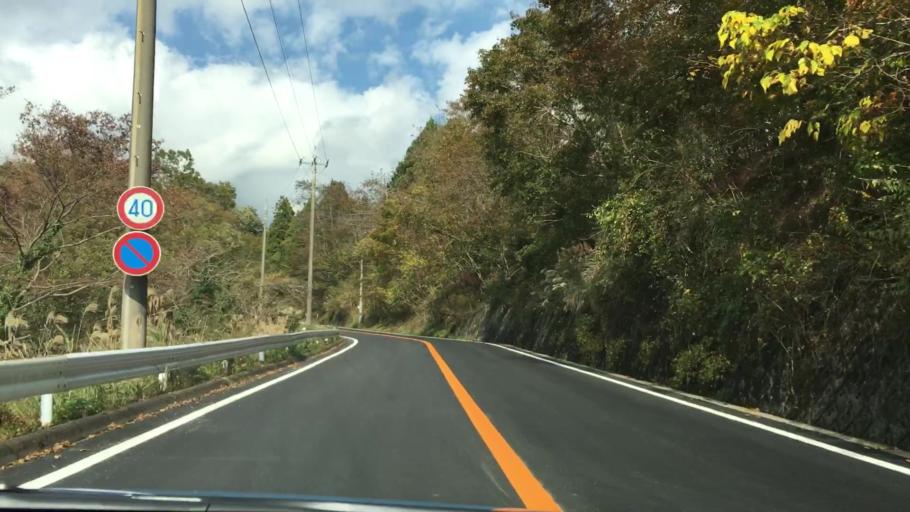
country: JP
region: Shizuoka
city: Gotemba
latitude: 35.3787
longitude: 138.9441
